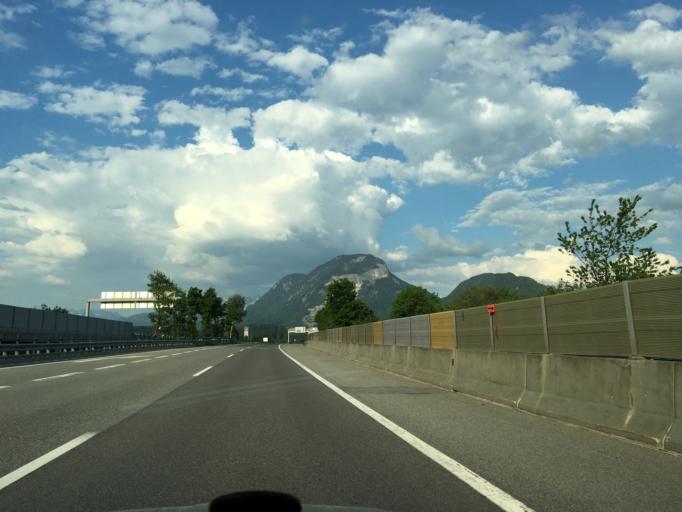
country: AT
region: Tyrol
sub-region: Politischer Bezirk Kufstein
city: Angath
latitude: 47.4957
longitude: 12.0644
